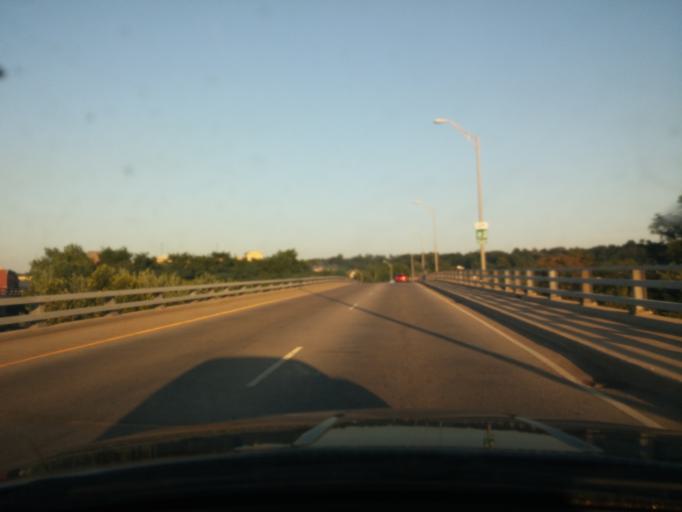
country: US
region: Indiana
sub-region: Tippecanoe County
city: West Lafayette
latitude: 40.4181
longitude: -86.8982
